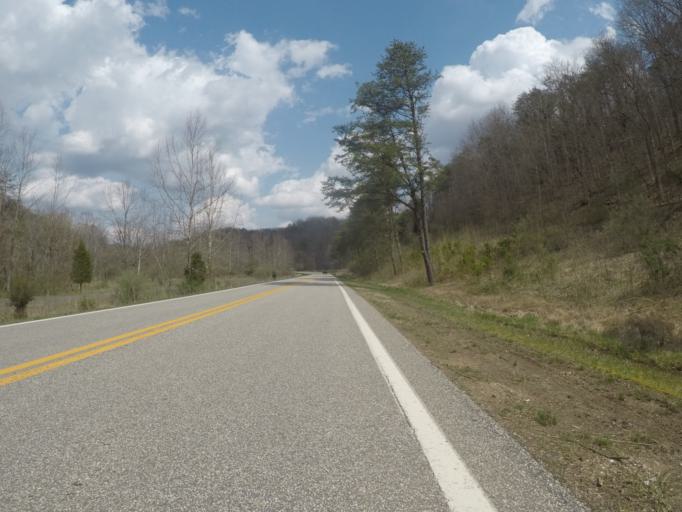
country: US
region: West Virginia
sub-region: Cabell County
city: Pea Ridge
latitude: 38.3096
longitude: -82.3408
